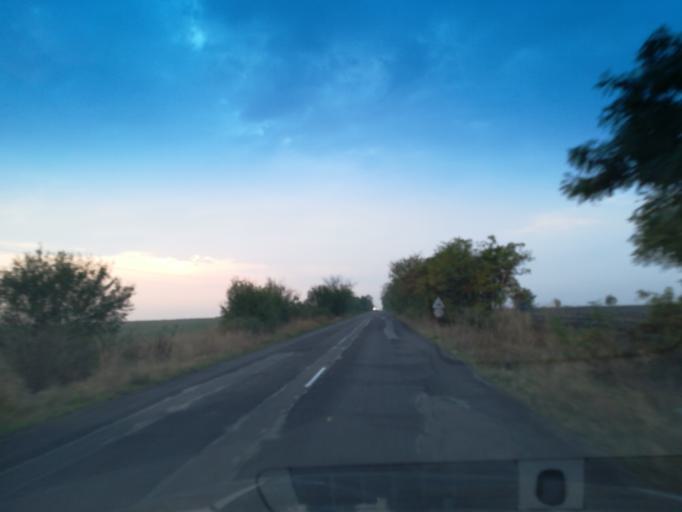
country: BG
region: Stara Zagora
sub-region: Obshtina Chirpan
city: Chirpan
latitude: 42.1803
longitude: 25.2364
